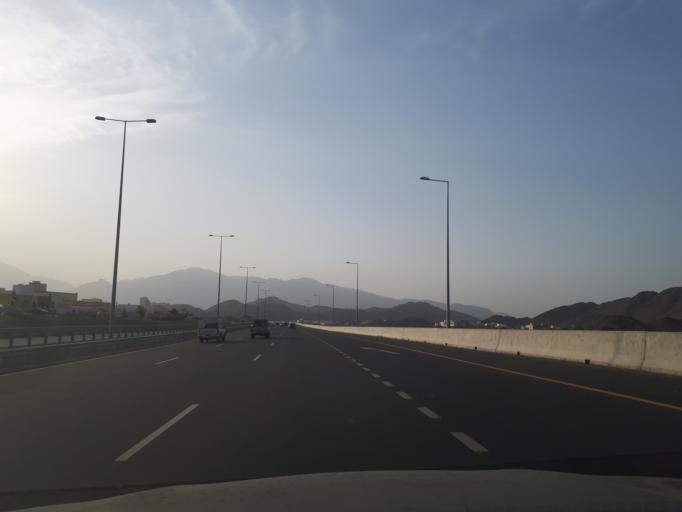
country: OM
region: Muhafazat ad Dakhiliyah
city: Bidbid
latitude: 23.3346
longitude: 58.1129
